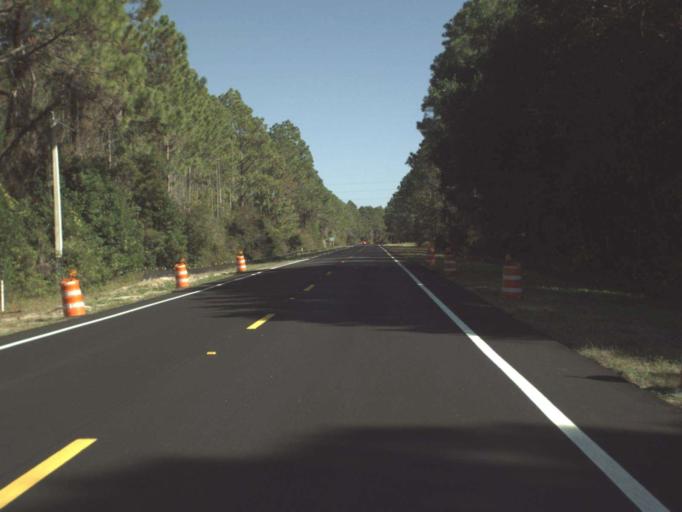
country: US
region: Florida
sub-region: Gulf County
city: Port Saint Joe
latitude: 29.7765
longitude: -85.2766
